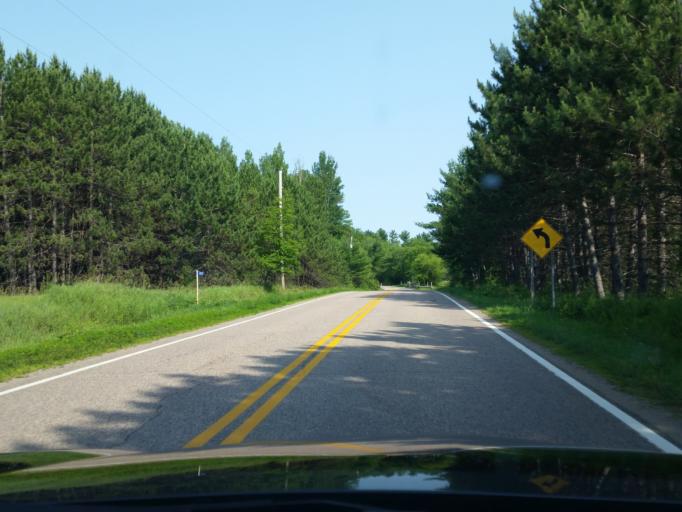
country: CA
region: Quebec
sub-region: Outaouais
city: Shawville
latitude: 45.5244
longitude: -76.4489
